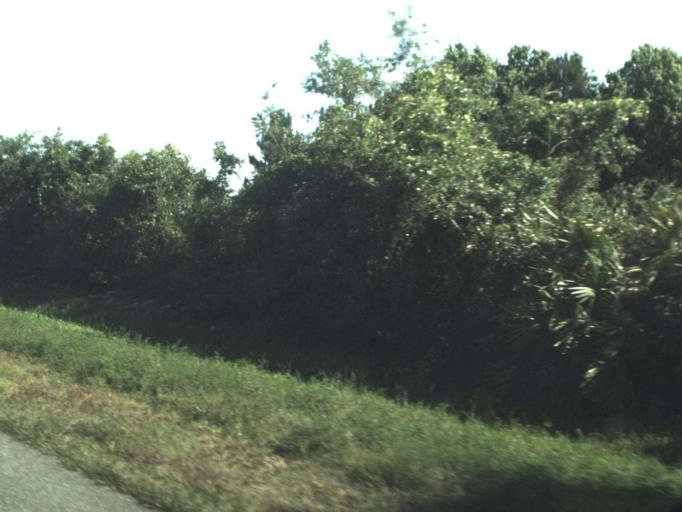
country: US
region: Florida
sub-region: Seminole County
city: Geneva
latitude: 28.7600
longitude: -81.1449
